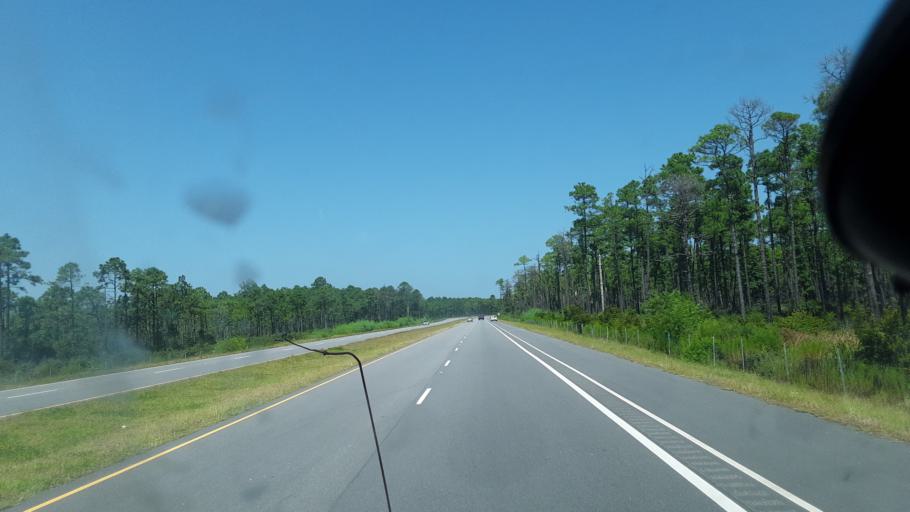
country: US
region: South Carolina
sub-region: Horry County
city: Myrtle Beach
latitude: 33.7890
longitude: -78.8797
